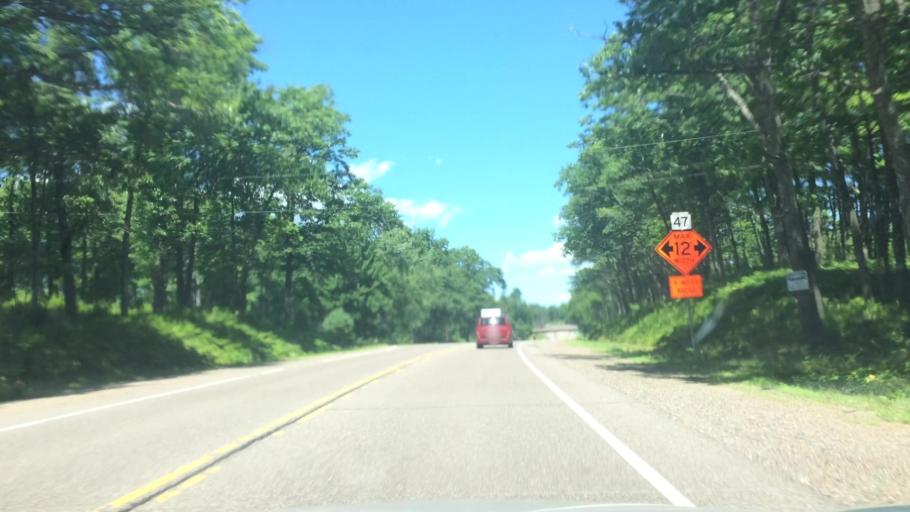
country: US
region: Wisconsin
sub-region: Vilas County
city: Lac du Flambeau
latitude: 45.7801
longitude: -89.7144
